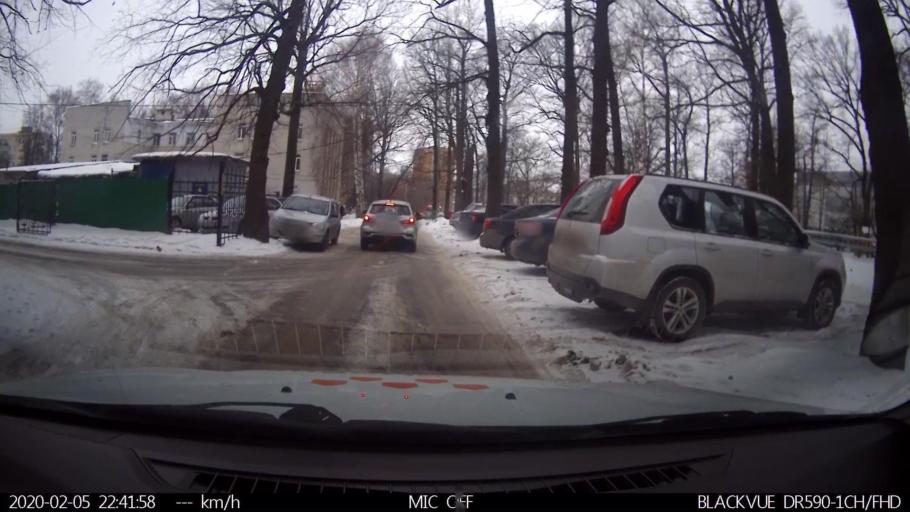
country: RU
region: Nizjnij Novgorod
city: Imeni Stepana Razina
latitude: 54.7193
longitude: 44.3479
